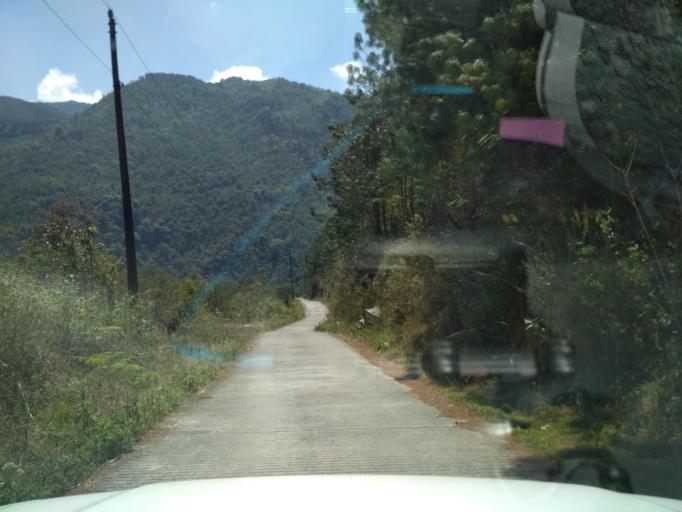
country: MX
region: Veracruz
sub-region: Tlilapan
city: Tonalixco
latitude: 18.7677
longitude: -97.0830
